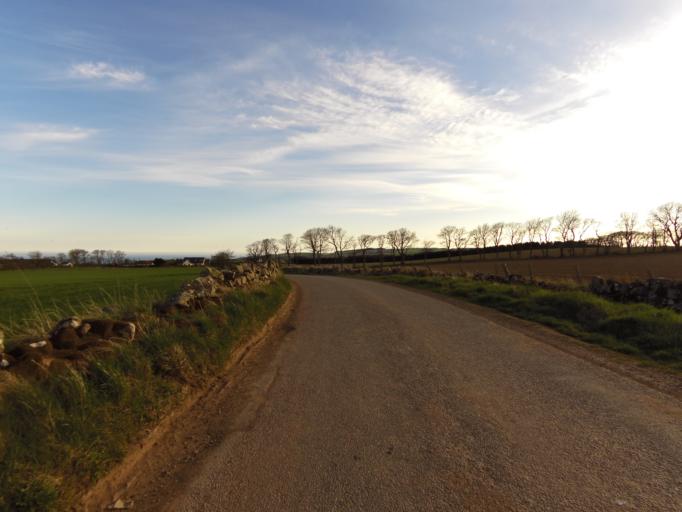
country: GB
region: Scotland
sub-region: Aberdeenshire
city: Stonehaven
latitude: 56.9099
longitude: -2.2131
